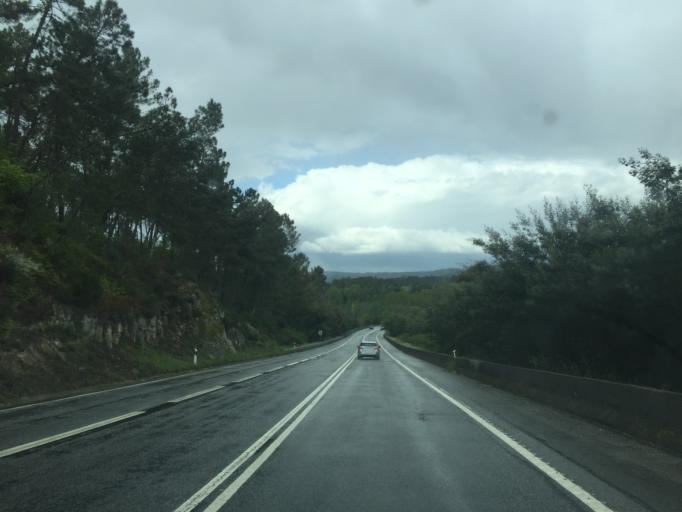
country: PT
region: Viseu
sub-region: Viseu
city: Abraveses
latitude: 40.6617
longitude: -8.0052
